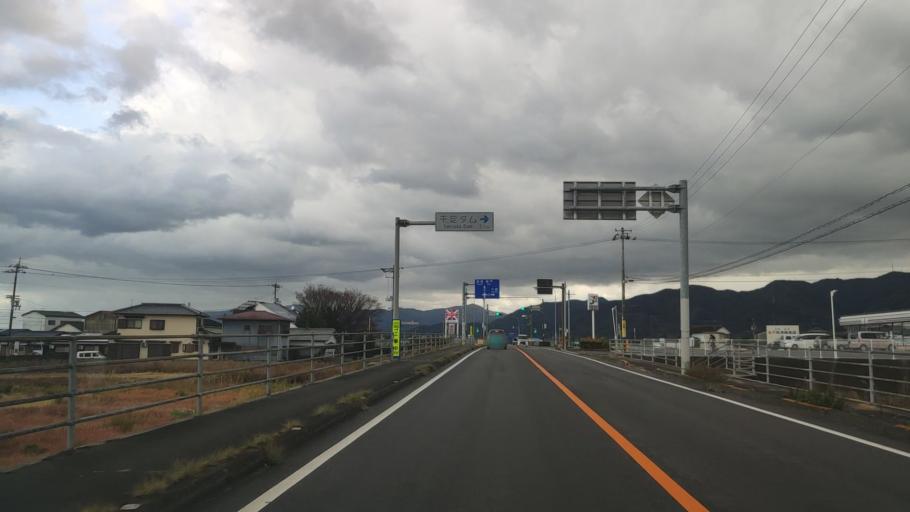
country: JP
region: Tokushima
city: Ishii
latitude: 34.2210
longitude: 134.4110
